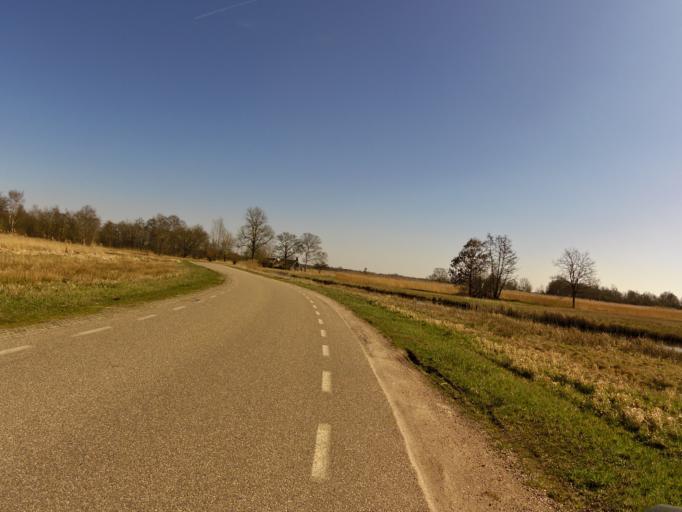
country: NL
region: Overijssel
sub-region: Gemeente Steenwijkerland
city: Oldemarkt
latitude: 52.7845
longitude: 5.9787
